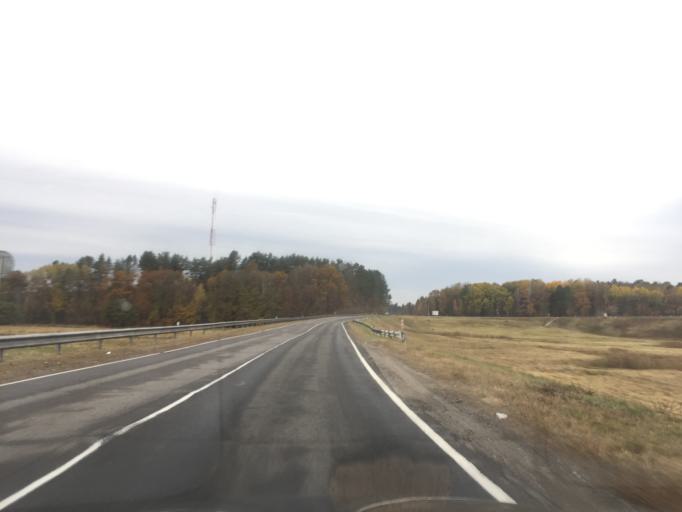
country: BY
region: Gomel
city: Gomel
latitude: 52.3870
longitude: 30.8317
